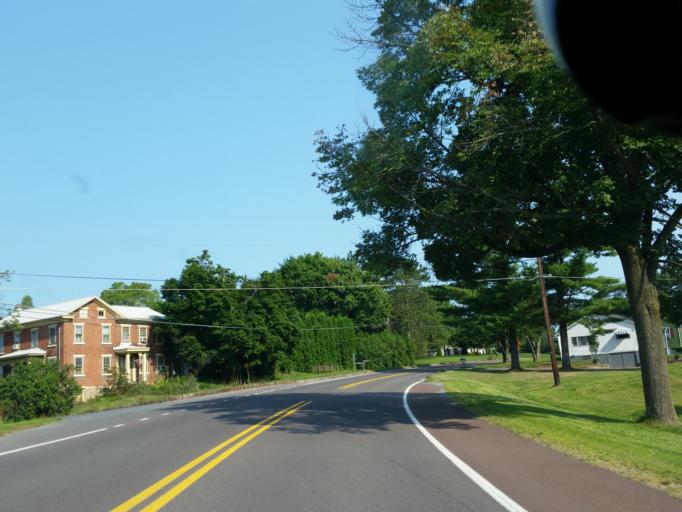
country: US
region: Pennsylvania
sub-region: Union County
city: New Columbia
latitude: 41.0452
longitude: -76.8823
